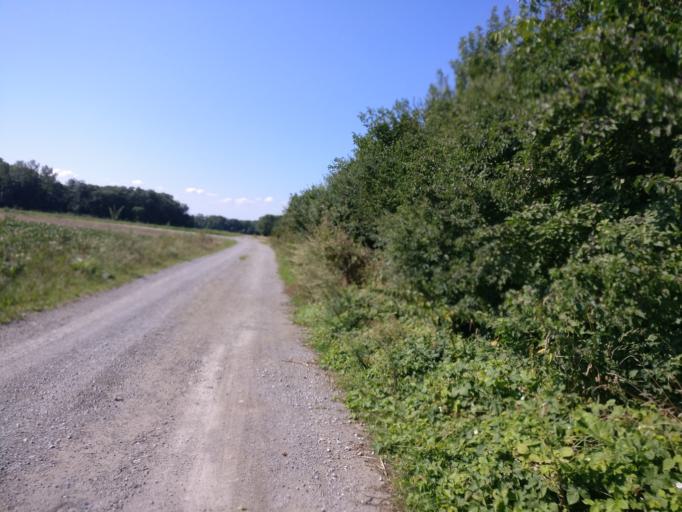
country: AT
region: Lower Austria
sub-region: Politischer Bezirk Baden
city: Ebreichsdorf
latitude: 47.9322
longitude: 16.3713
